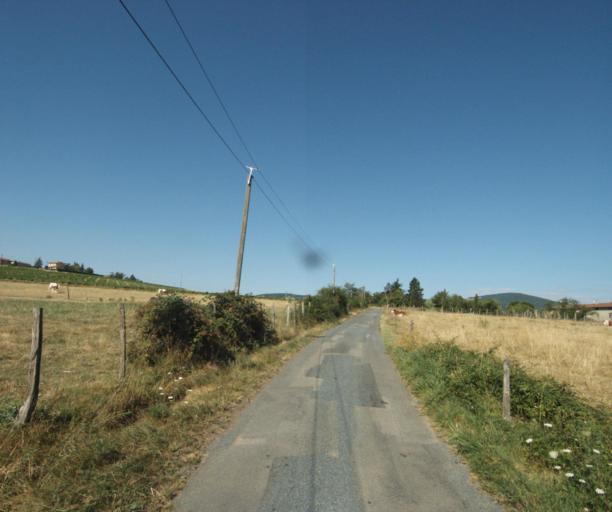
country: FR
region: Rhone-Alpes
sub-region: Departement du Rhone
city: Sain-Bel
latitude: 45.8070
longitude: 4.5863
